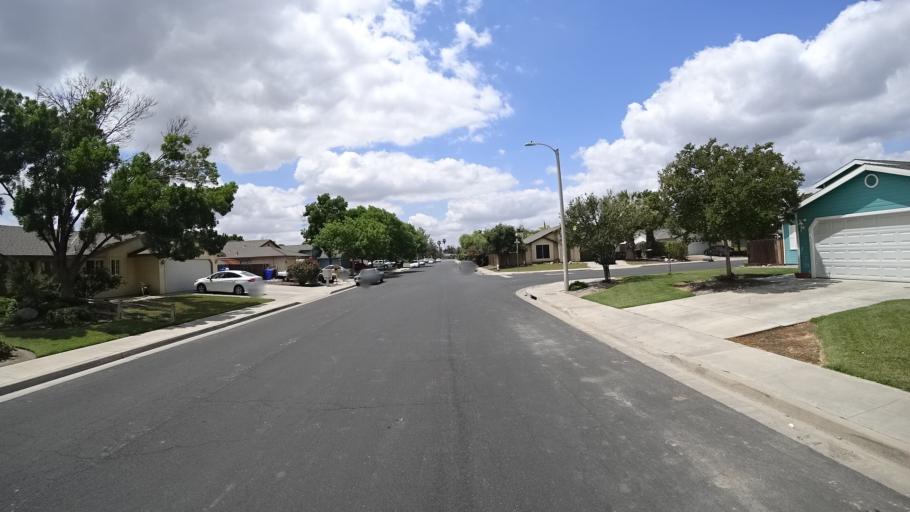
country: US
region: California
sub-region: Kings County
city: Hanford
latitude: 36.3119
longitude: -119.6577
